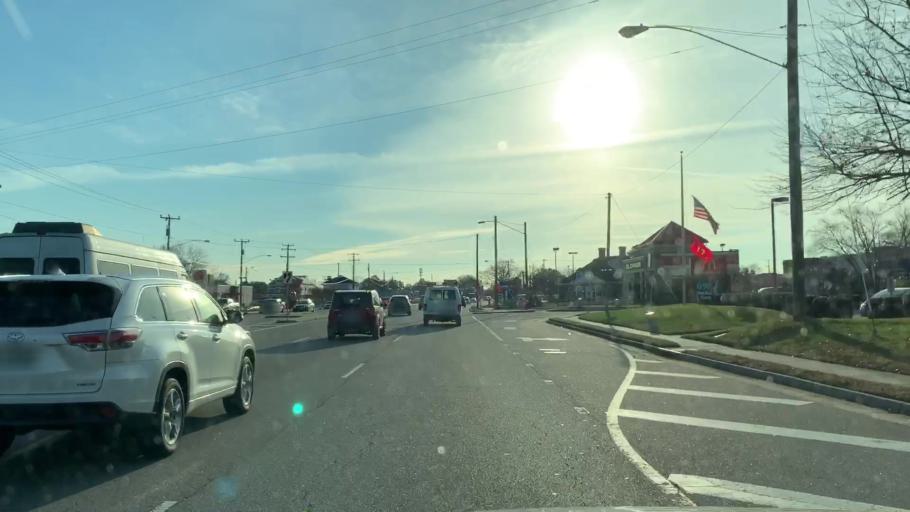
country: US
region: Virginia
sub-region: City of Chesapeake
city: Chesapeake
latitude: 36.7989
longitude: -76.1779
